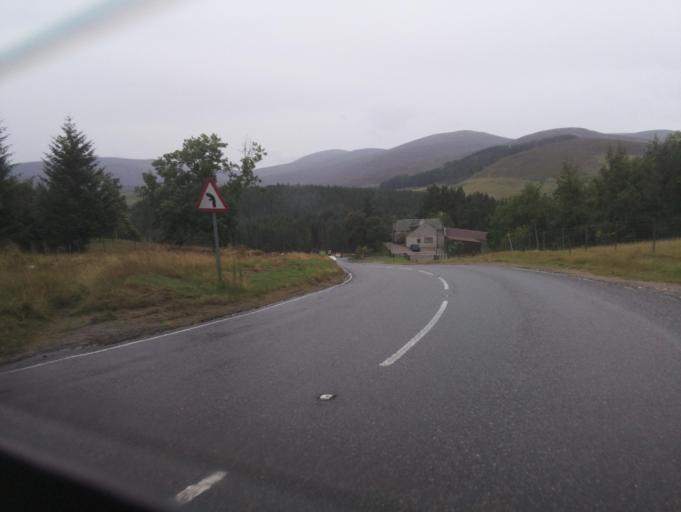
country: GB
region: Scotland
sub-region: Aberdeenshire
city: Ballater
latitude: 57.1697
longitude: -3.2316
